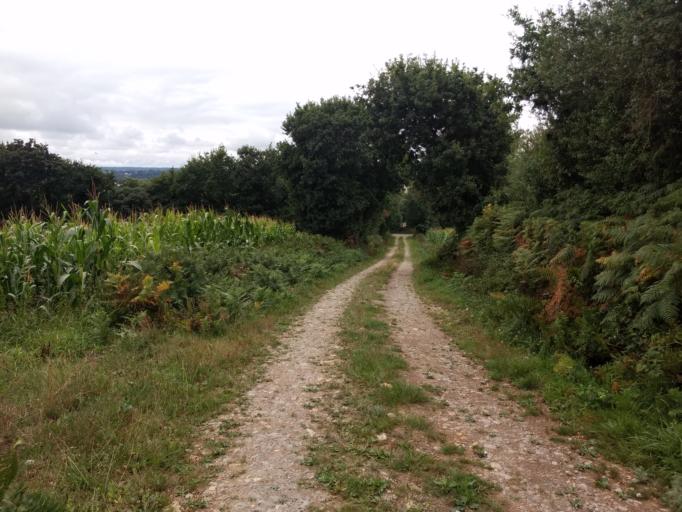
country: FR
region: Brittany
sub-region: Departement du Finistere
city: Loperhet
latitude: 48.3588
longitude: -4.2930
